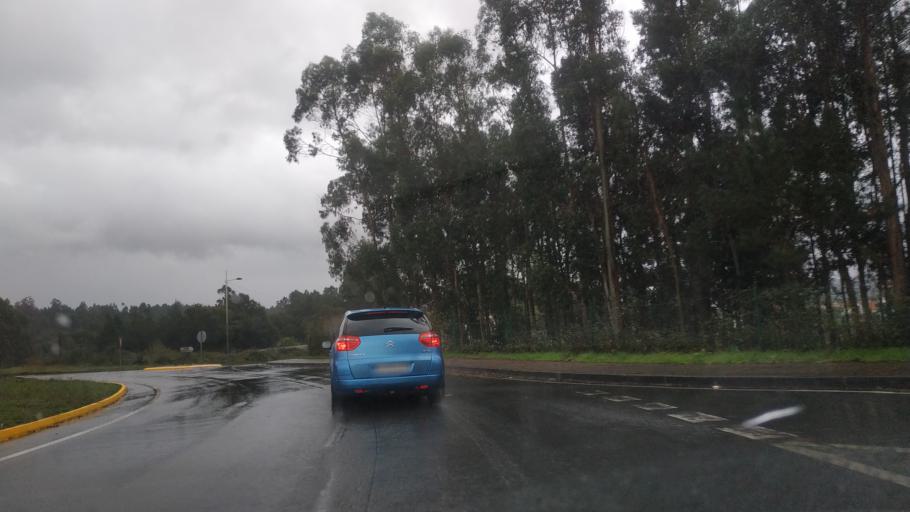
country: ES
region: Galicia
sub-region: Provincia da Coruna
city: Negreira
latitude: 42.9199
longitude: -8.7345
